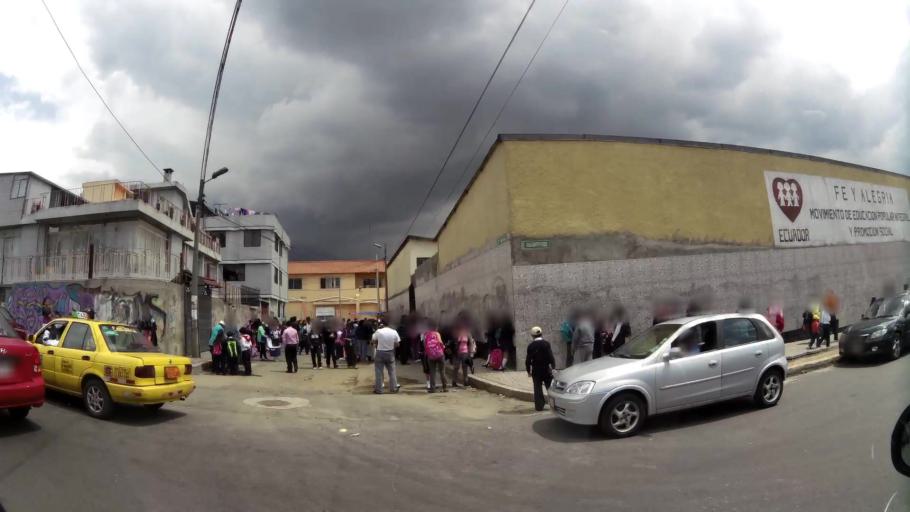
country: EC
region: Pichincha
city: Quito
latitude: -0.2513
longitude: -78.5166
